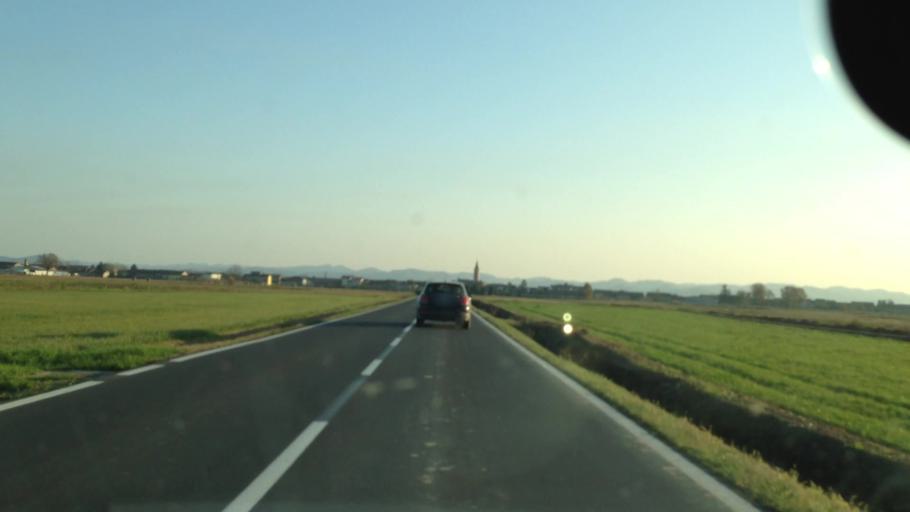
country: IT
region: Piedmont
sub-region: Provincia di Vercelli
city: Lamporo
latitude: 45.2387
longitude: 8.0935
